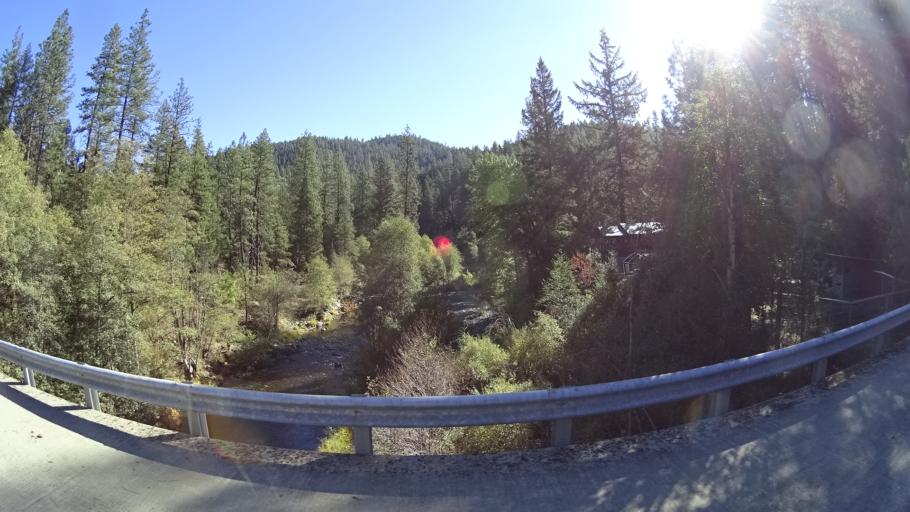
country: US
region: California
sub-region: Trinity County
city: Weaverville
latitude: 41.1395
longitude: -123.1295
